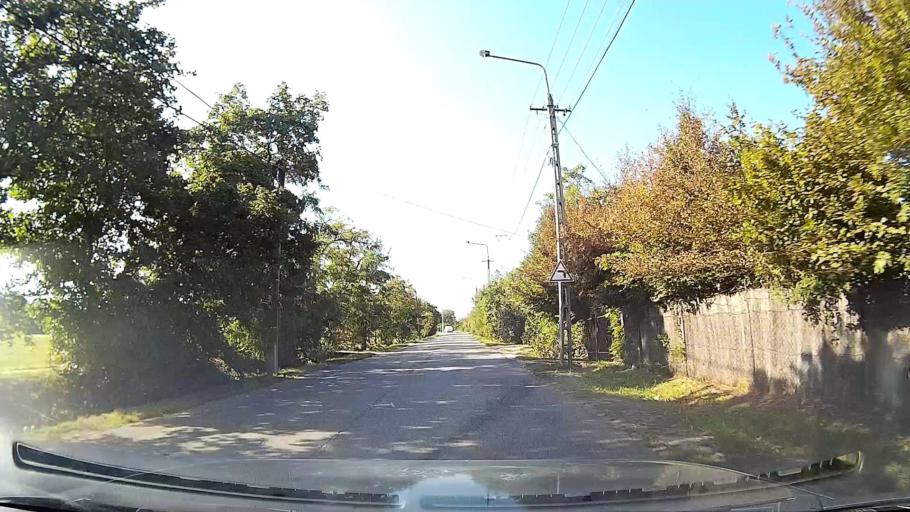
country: HU
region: Budapest
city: Budapest XXII. keruelet
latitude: 47.4221
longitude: 19.0054
